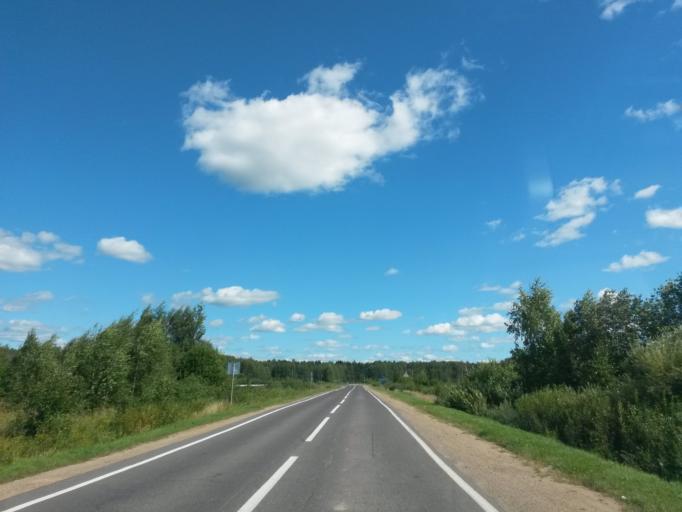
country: RU
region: Jaroslavl
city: Konstantinovskiy
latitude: 57.8043
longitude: 39.7668
